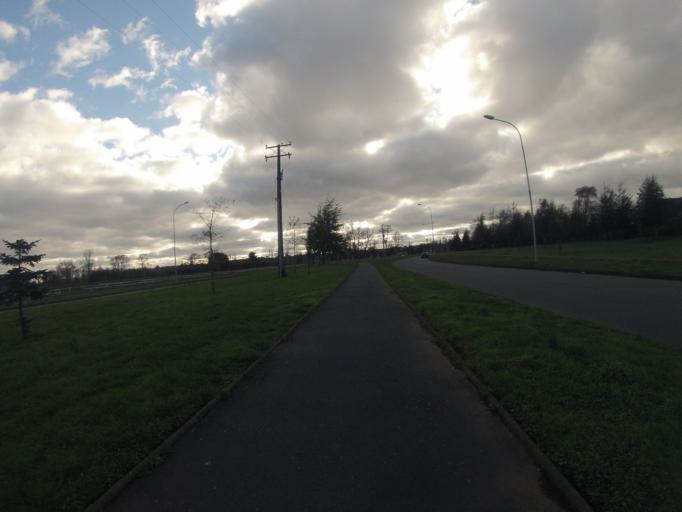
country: CL
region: Araucania
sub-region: Provincia de Cautin
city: Temuco
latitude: -38.7466
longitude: -72.6475
